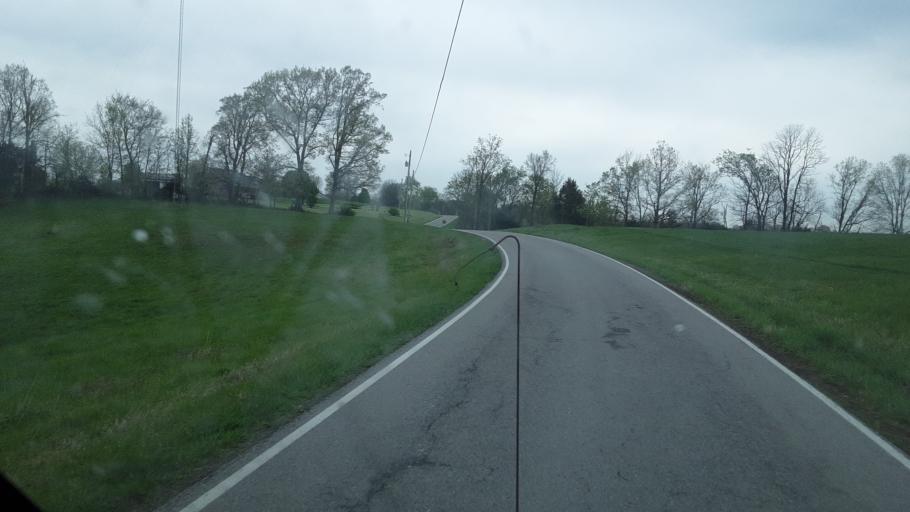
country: US
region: Kentucky
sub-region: Owen County
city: Owenton
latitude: 38.6479
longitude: -84.7726
